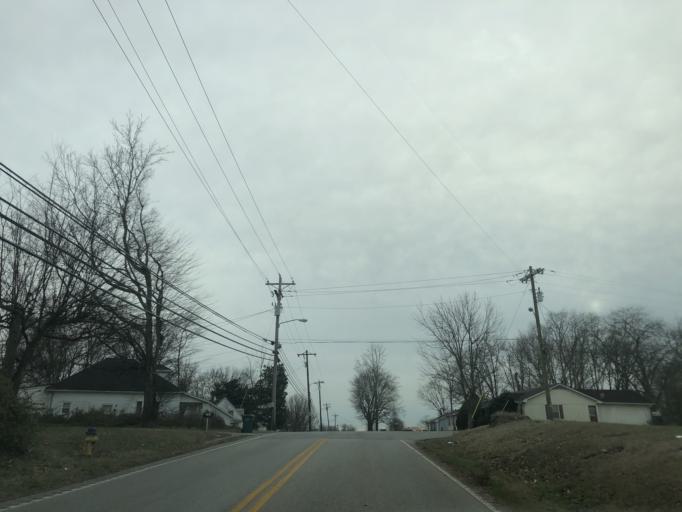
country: US
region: Tennessee
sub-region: Wilson County
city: Lebanon
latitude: 36.2192
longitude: -86.2809
